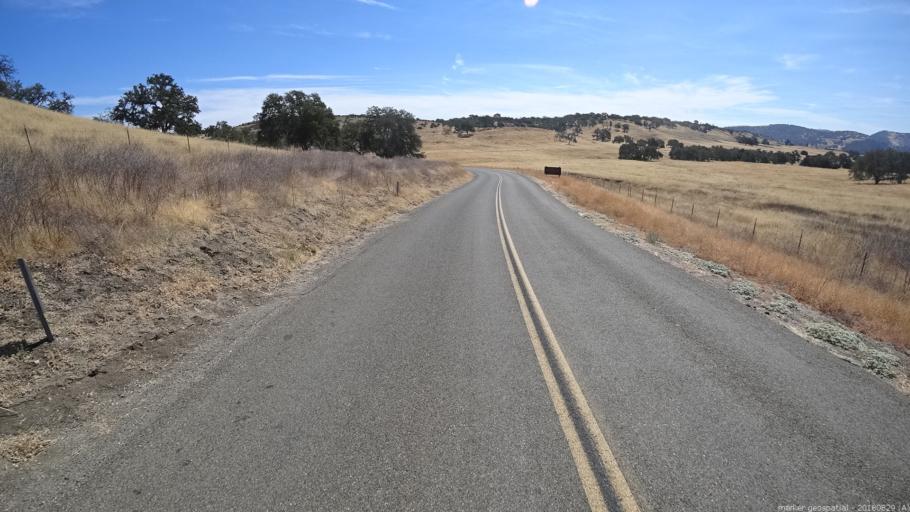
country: US
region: California
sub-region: San Luis Obispo County
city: Lake Nacimiento
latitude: 35.8283
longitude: -120.9784
